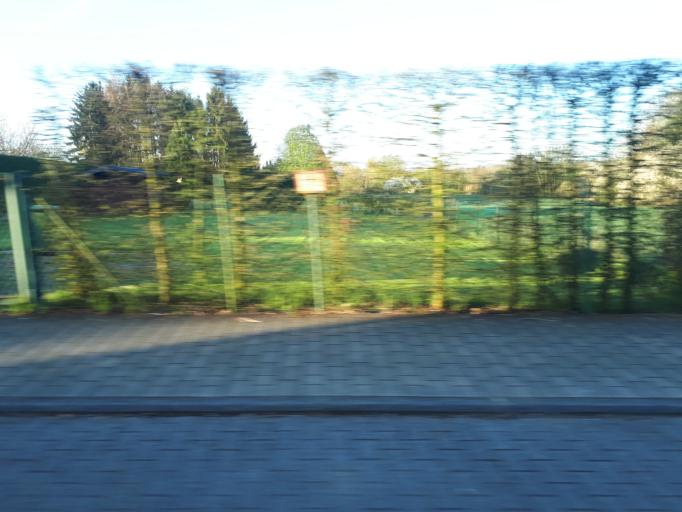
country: LU
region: Luxembourg
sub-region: Canton de Luxembourg
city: Strassen
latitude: 49.6171
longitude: 6.0848
